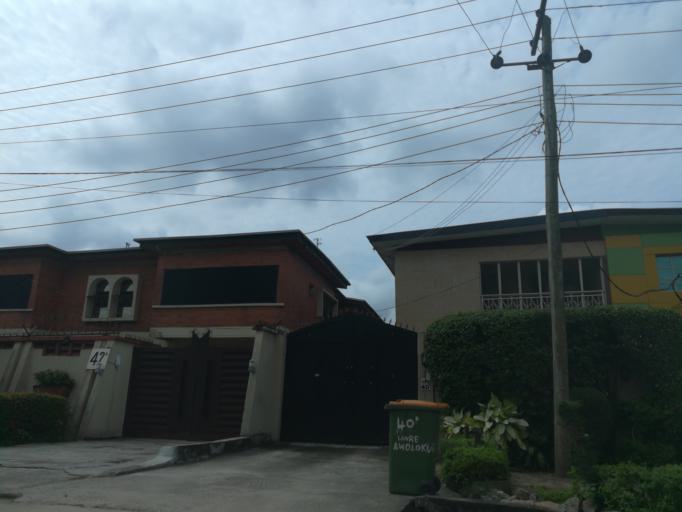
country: NG
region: Lagos
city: Somolu
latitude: 6.5472
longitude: 3.3863
